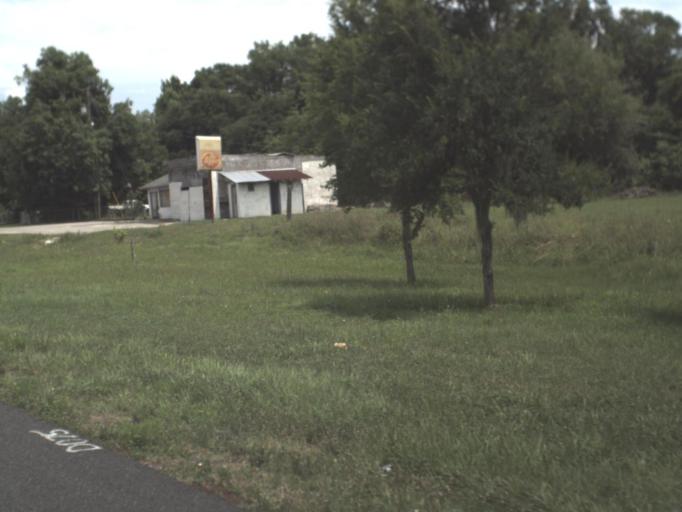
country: US
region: Florida
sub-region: Alachua County
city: Gainesville
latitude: 29.6137
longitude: -82.2543
